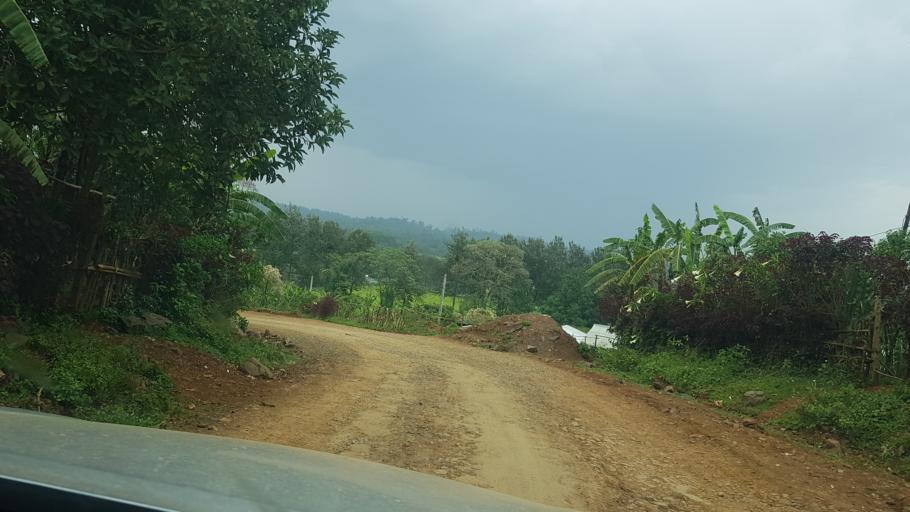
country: ET
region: Oromiya
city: Gore
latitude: 7.8359
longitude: 35.4718
